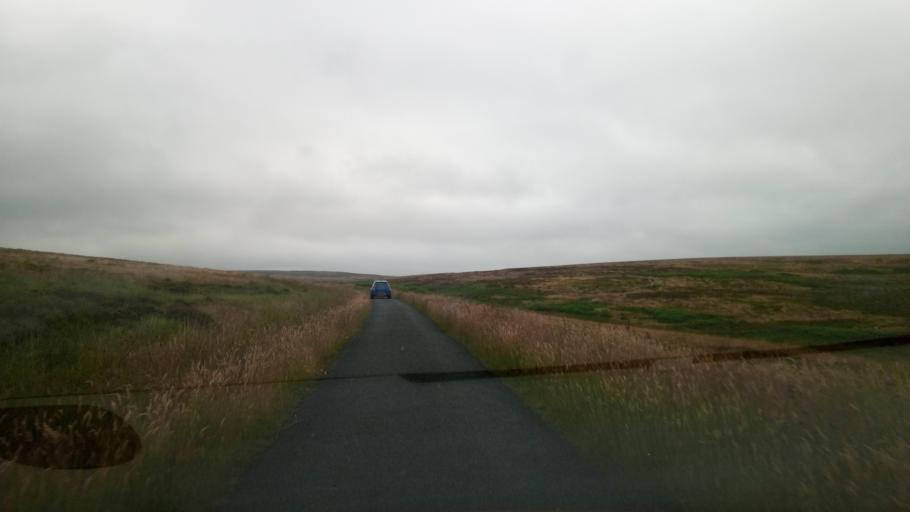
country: GB
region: Scotland
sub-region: Dumfries and Galloway
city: Langholm
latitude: 55.1706
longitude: -2.9200
